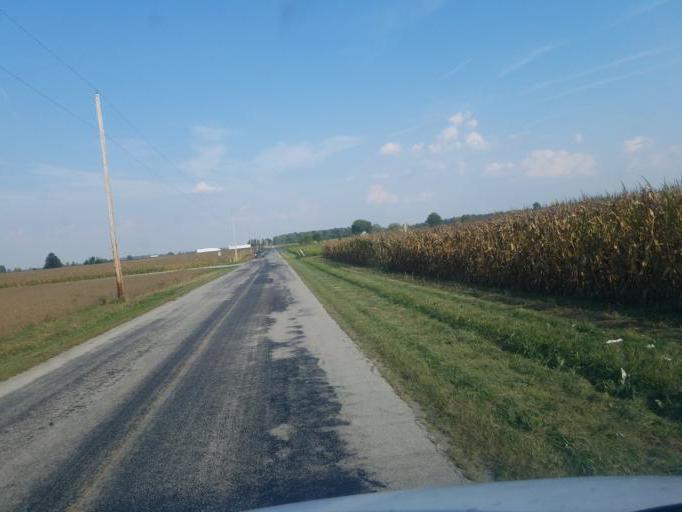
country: US
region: Ohio
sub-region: Wyandot County
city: Carey
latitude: 40.9051
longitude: -83.4492
